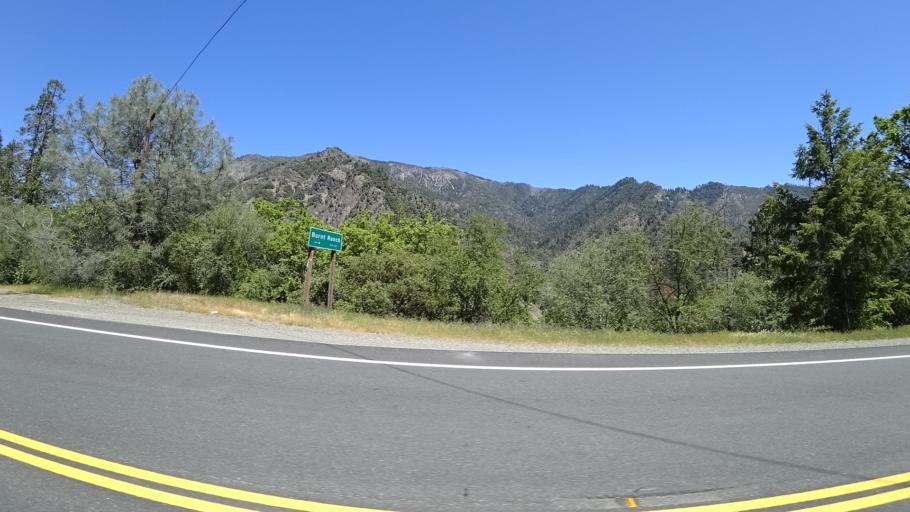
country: US
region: California
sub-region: Humboldt County
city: Willow Creek
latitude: 40.8069
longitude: -123.4713
